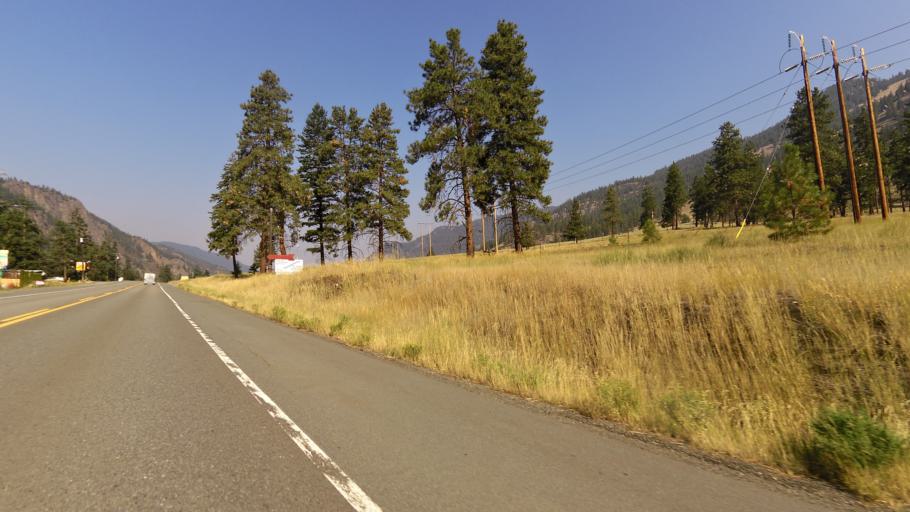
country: CA
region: British Columbia
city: Princeton
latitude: 49.3667
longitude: -120.1257
